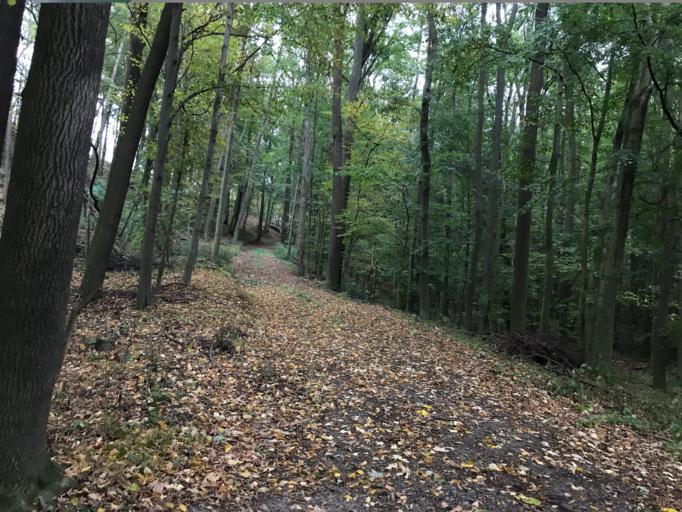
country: DE
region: Saxony
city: Seelitz
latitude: 51.0211
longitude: 12.8400
